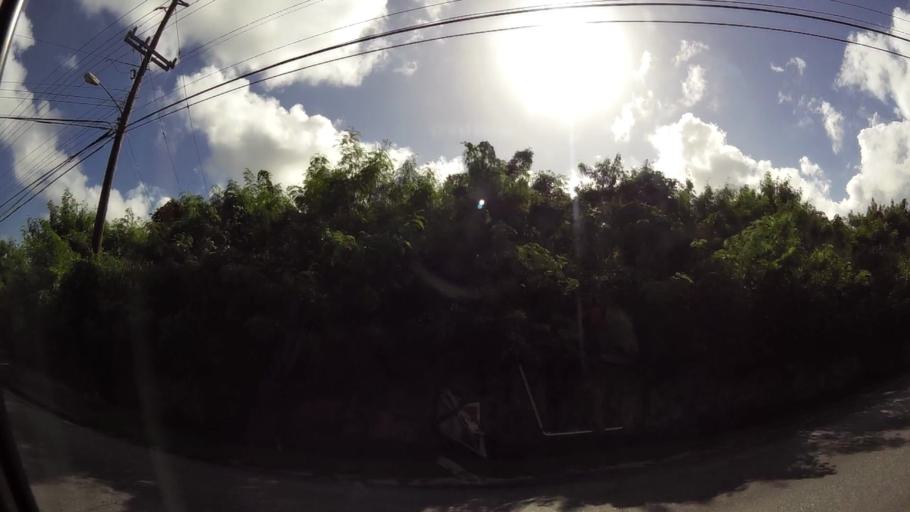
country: BB
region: Saint James
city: Holetown
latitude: 13.1806
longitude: -59.6138
